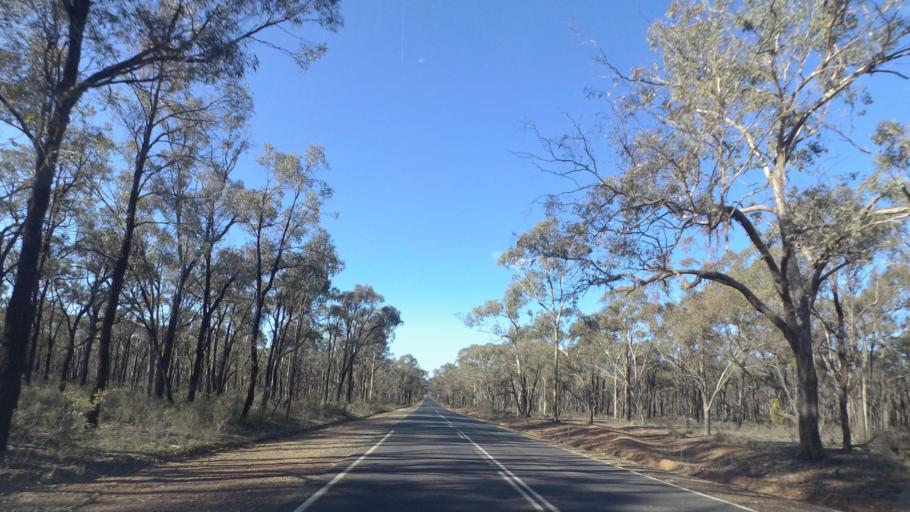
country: AU
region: Victoria
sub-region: Greater Bendigo
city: Epsom
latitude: -36.6645
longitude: 144.4440
